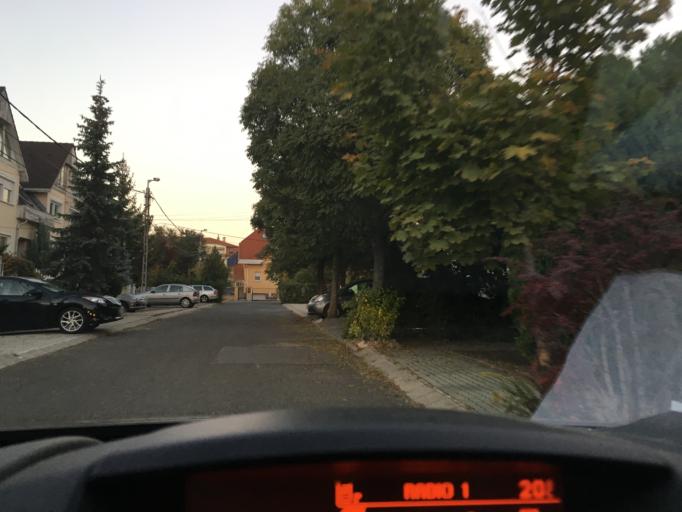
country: HU
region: Budapest
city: Budapest XVII. keruelet
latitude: 47.4773
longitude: 19.2324
